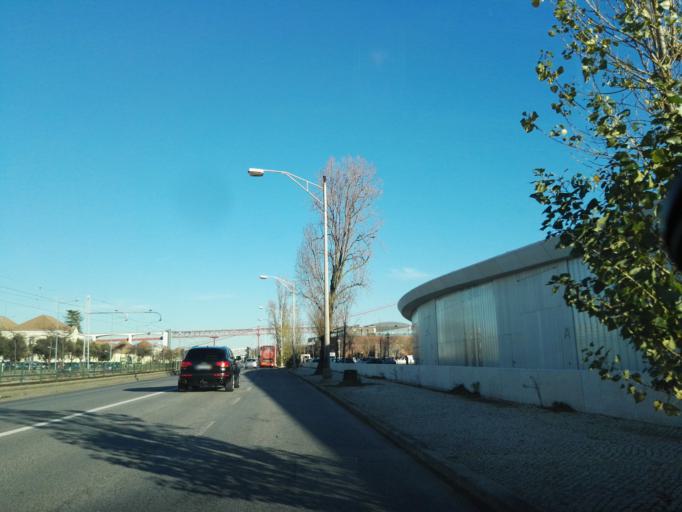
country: PT
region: Setubal
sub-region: Almada
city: Caparica
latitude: 38.6963
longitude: -9.1941
